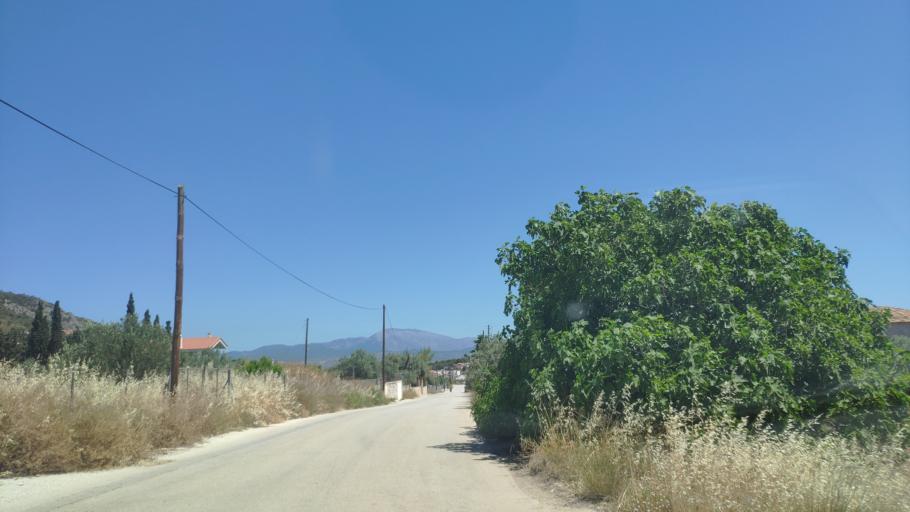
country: GR
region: Peloponnese
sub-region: Nomos Korinthias
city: Loutra Oraias Elenis
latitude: 37.8584
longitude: 22.9904
